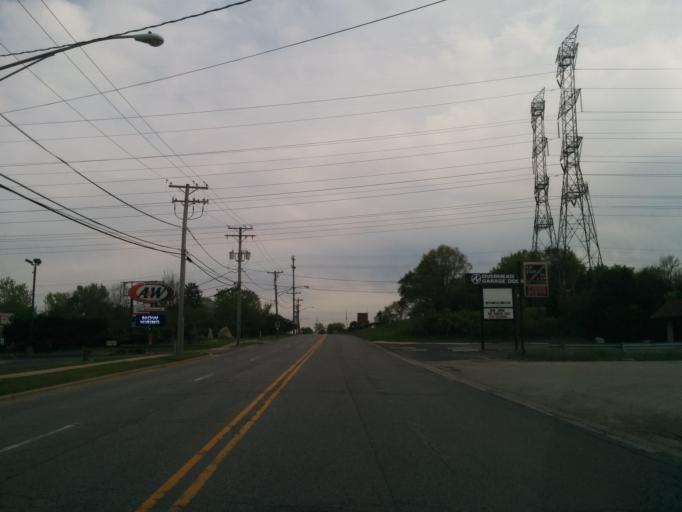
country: US
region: Illinois
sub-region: Kane County
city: North Aurora
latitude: 41.8037
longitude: -88.3264
